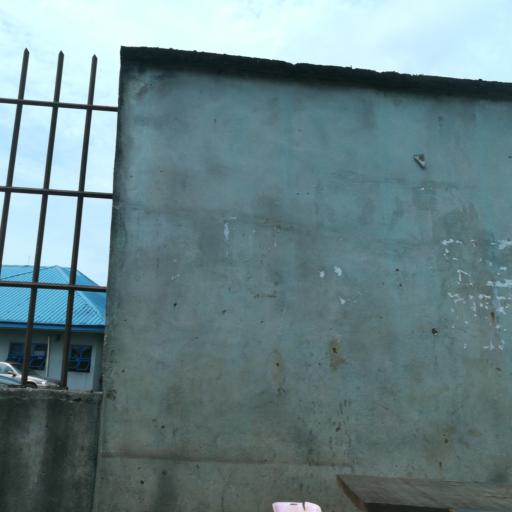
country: NG
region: Rivers
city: Port Harcourt
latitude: 4.7943
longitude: 7.0277
